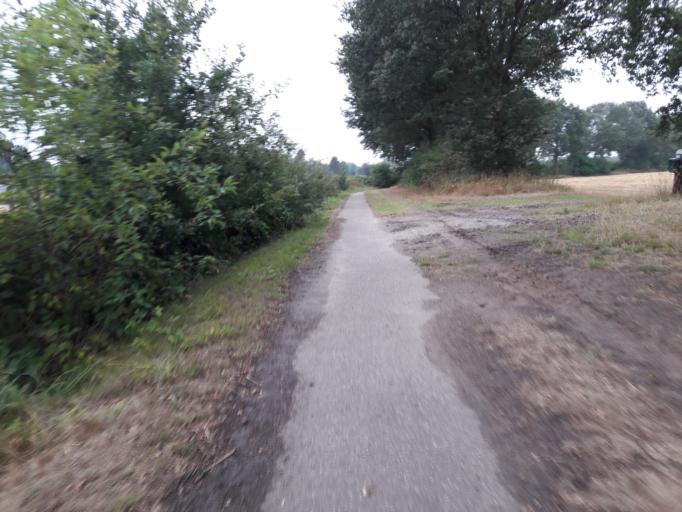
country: NL
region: Drenthe
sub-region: Gemeente Borger-Odoorn
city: Borger
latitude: 52.9285
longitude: 6.8109
